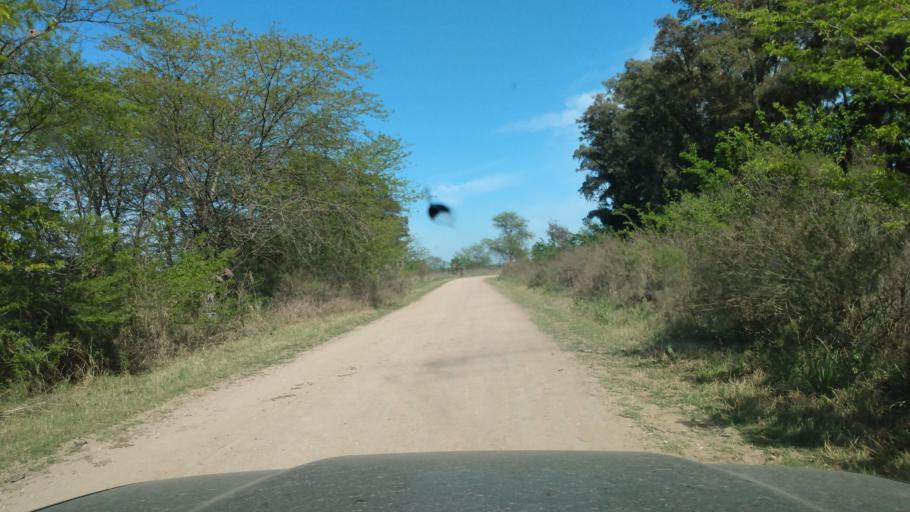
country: AR
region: Buenos Aires
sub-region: Partido de Lujan
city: Lujan
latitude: -34.6294
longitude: -59.1027
